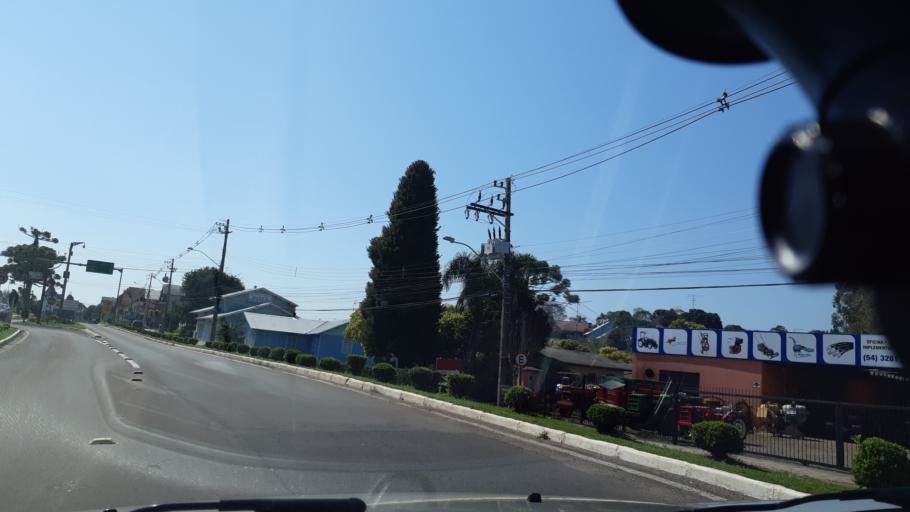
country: BR
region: Rio Grande do Sul
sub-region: Nova Petropolis
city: Nova Petropolis
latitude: -29.3868
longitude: -51.1241
